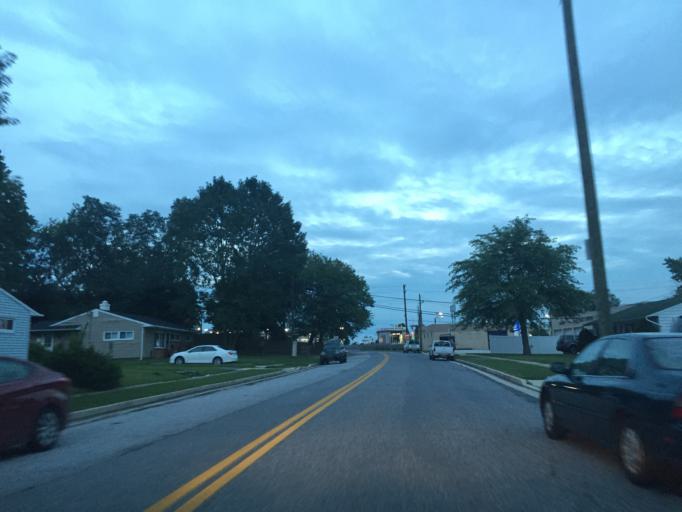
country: US
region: Maryland
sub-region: Baltimore County
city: Carney
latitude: 39.3905
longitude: -76.5304
